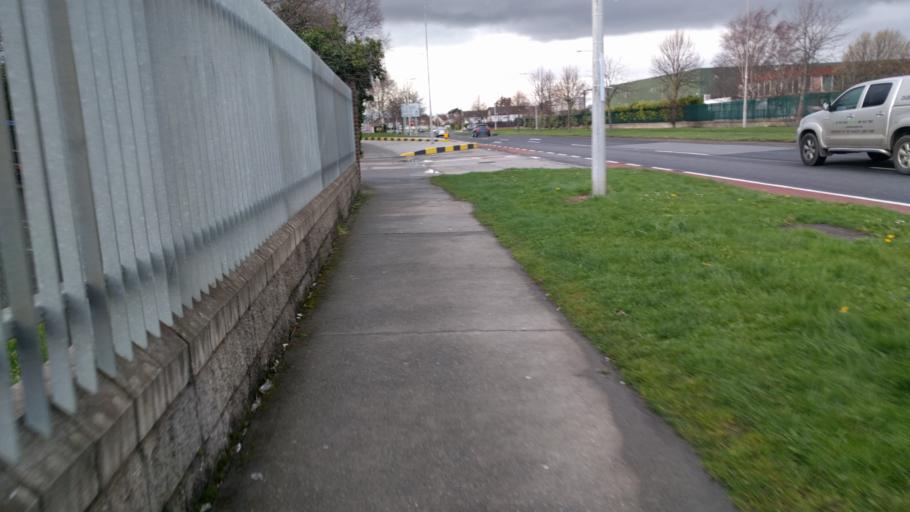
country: IE
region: Leinster
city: Tallaght
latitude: 53.2961
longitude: -6.3701
